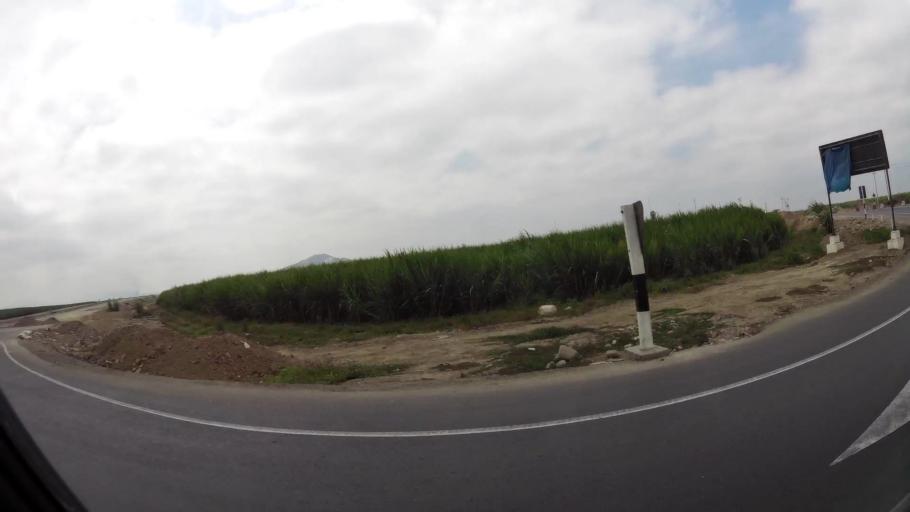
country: PE
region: La Libertad
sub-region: Ascope
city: Chocope
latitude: -7.7894
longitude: -79.2311
